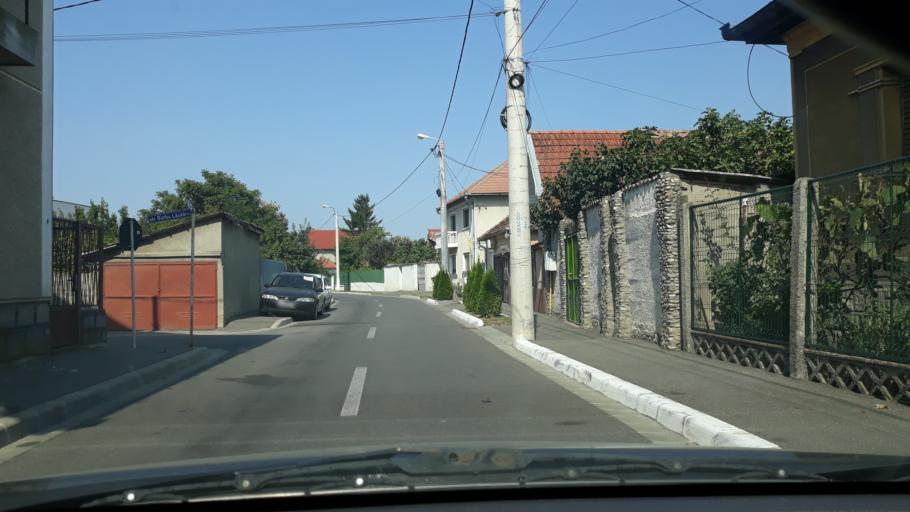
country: RO
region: Bihor
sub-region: Comuna Biharea
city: Oradea
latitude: 47.0414
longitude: 21.9517
